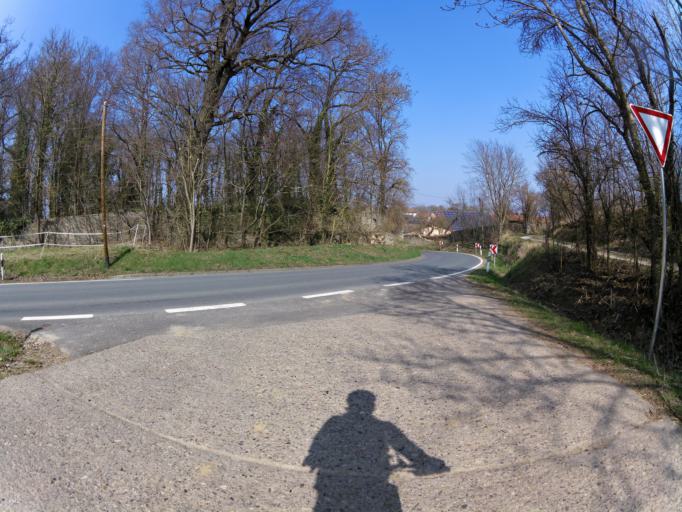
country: DE
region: Bavaria
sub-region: Regierungsbezirk Unterfranken
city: Gaukonigshofen
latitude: 49.6728
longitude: 9.9939
